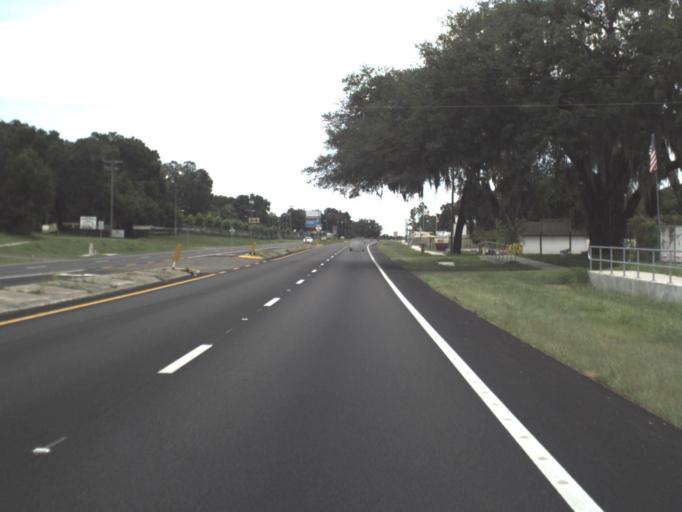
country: US
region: Florida
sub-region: Pasco County
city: Dade City North
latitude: 28.3886
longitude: -82.1939
